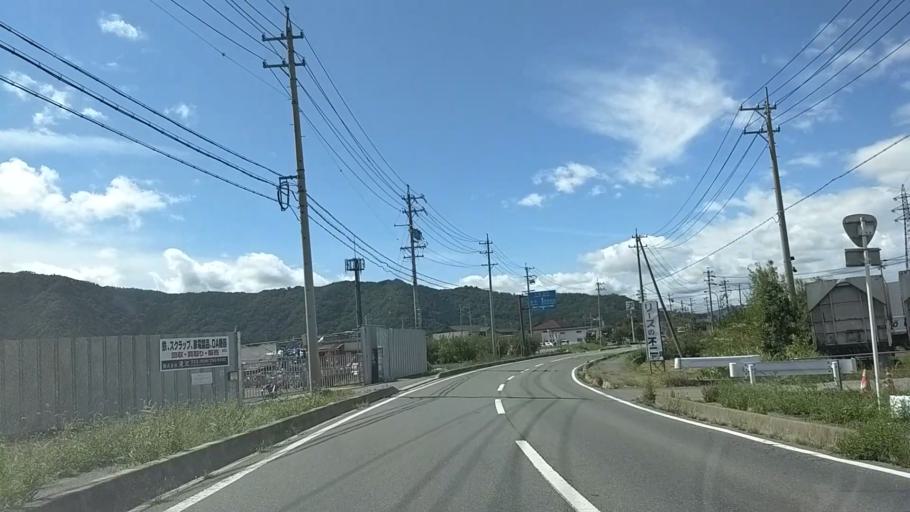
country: JP
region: Nagano
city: Nagano-shi
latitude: 36.6096
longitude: 138.2475
